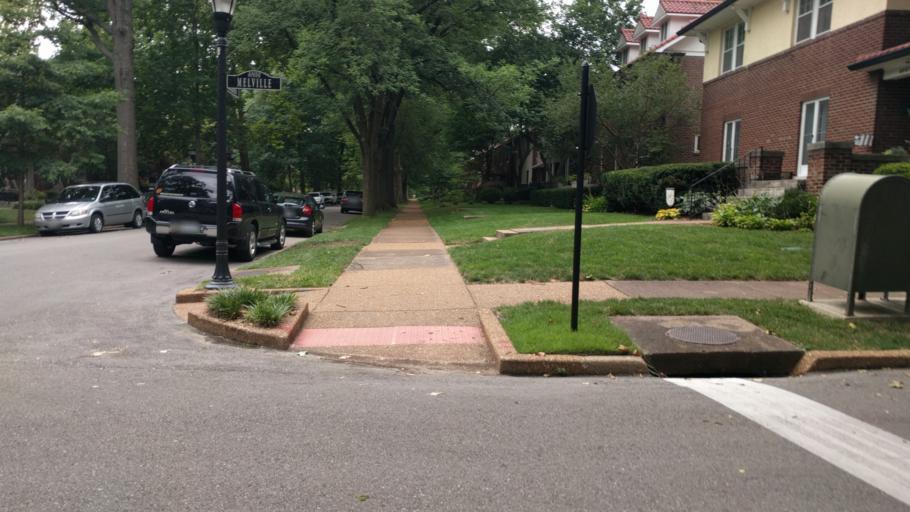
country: US
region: Missouri
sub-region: Saint Louis County
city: University City
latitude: 38.6516
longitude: -90.3074
